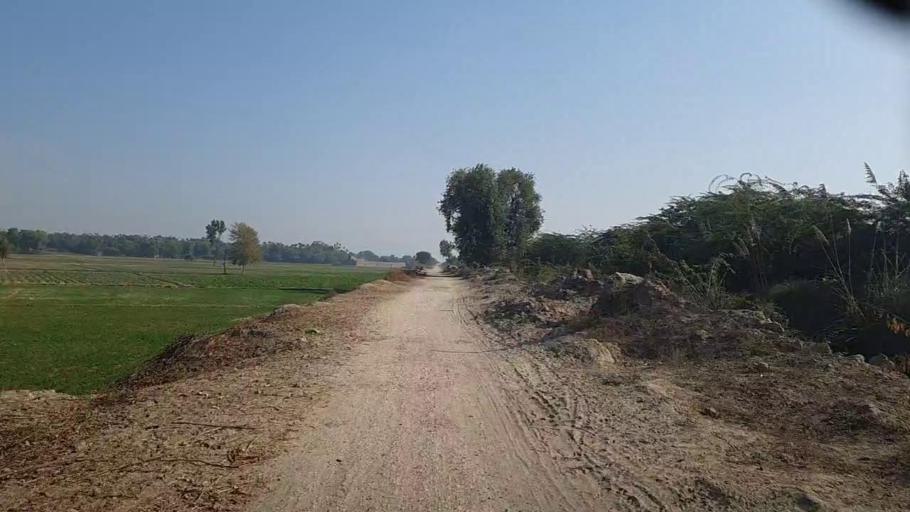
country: PK
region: Sindh
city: Darya Khan Marri
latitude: 26.7087
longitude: 68.3242
